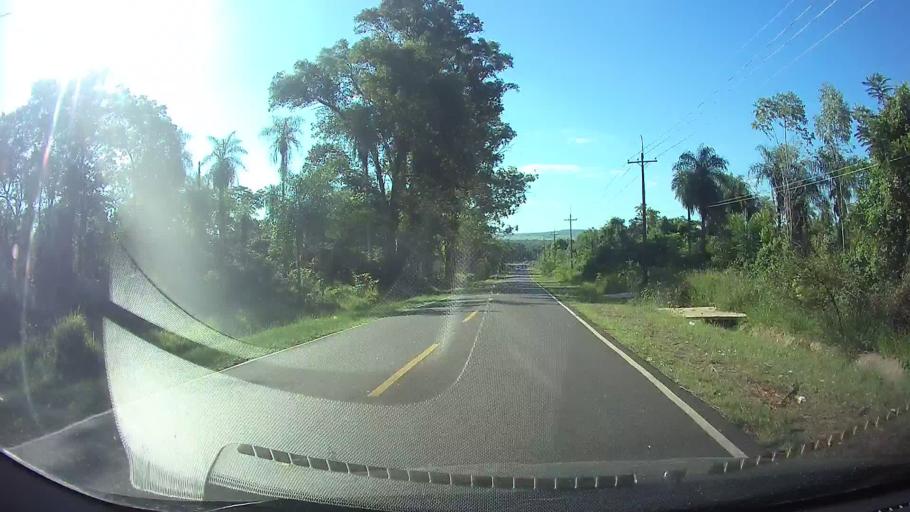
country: PY
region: Cordillera
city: Atyra
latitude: -25.3082
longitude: -57.1539
